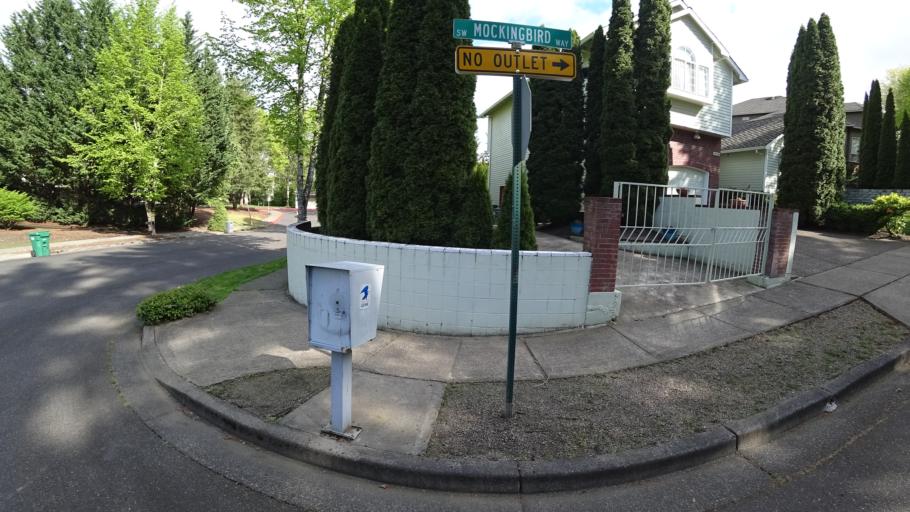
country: US
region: Oregon
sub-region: Washington County
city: Beaverton
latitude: 45.4456
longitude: -122.8289
